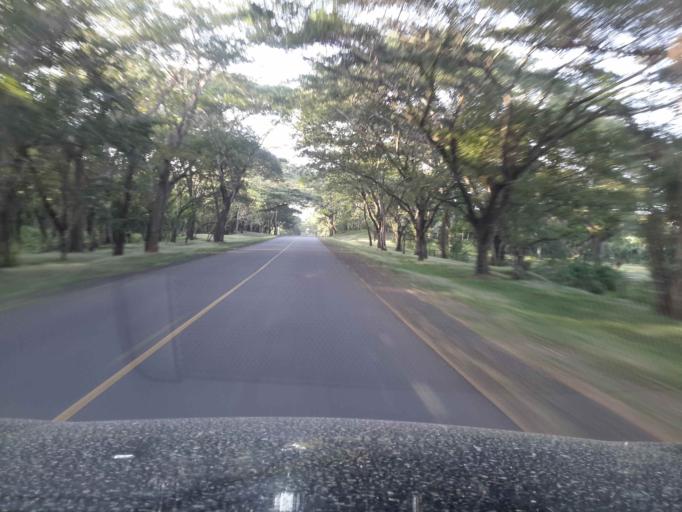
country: NI
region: Rio San Juan
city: San Miguelito
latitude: 11.4164
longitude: -84.8415
